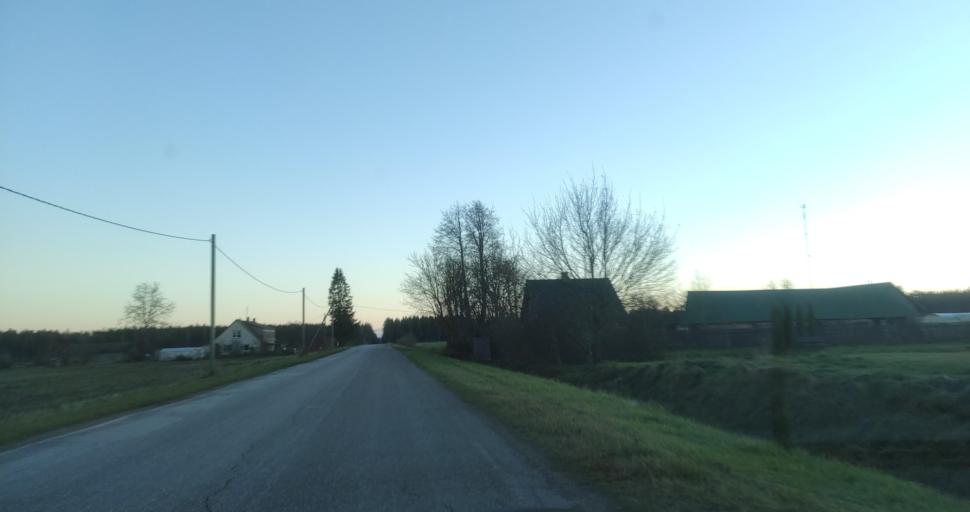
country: LV
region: Dundaga
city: Dundaga
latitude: 57.3741
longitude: 22.2310
